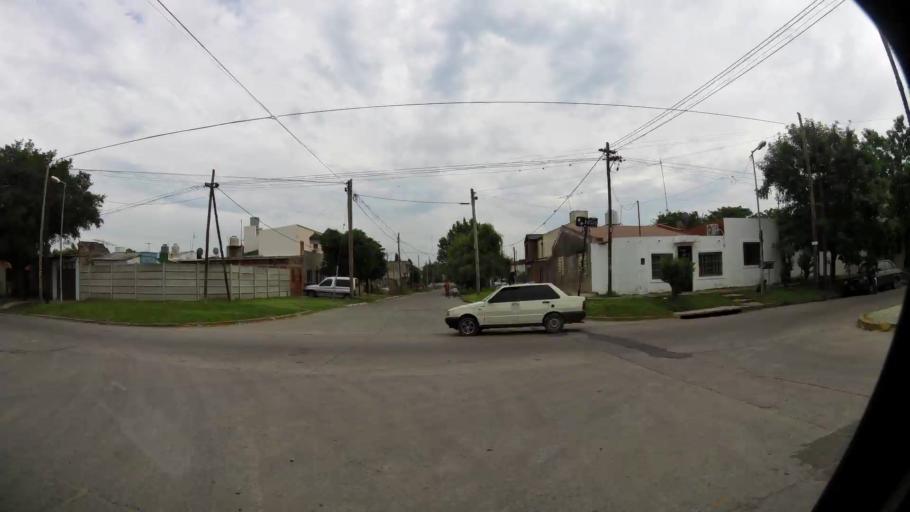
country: AR
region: Buenos Aires
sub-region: Partido de La Plata
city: La Plata
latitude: -34.9160
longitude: -57.9982
